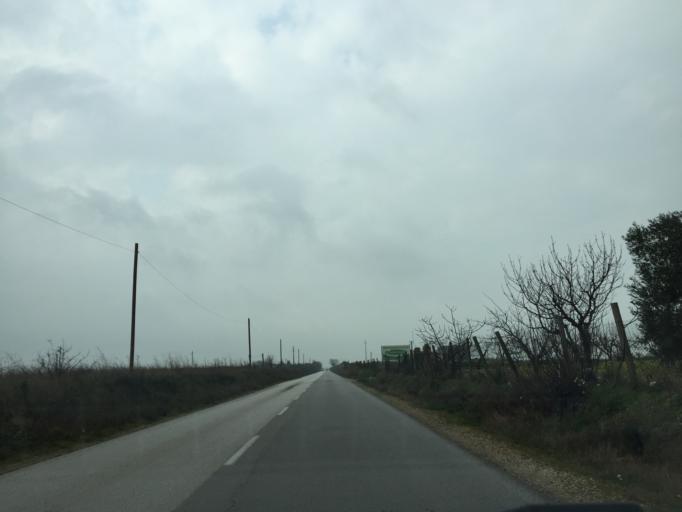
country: IT
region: Apulia
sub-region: Provincia di Foggia
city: Castelluccio dei Sauri
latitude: 41.4034
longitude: 15.4350
